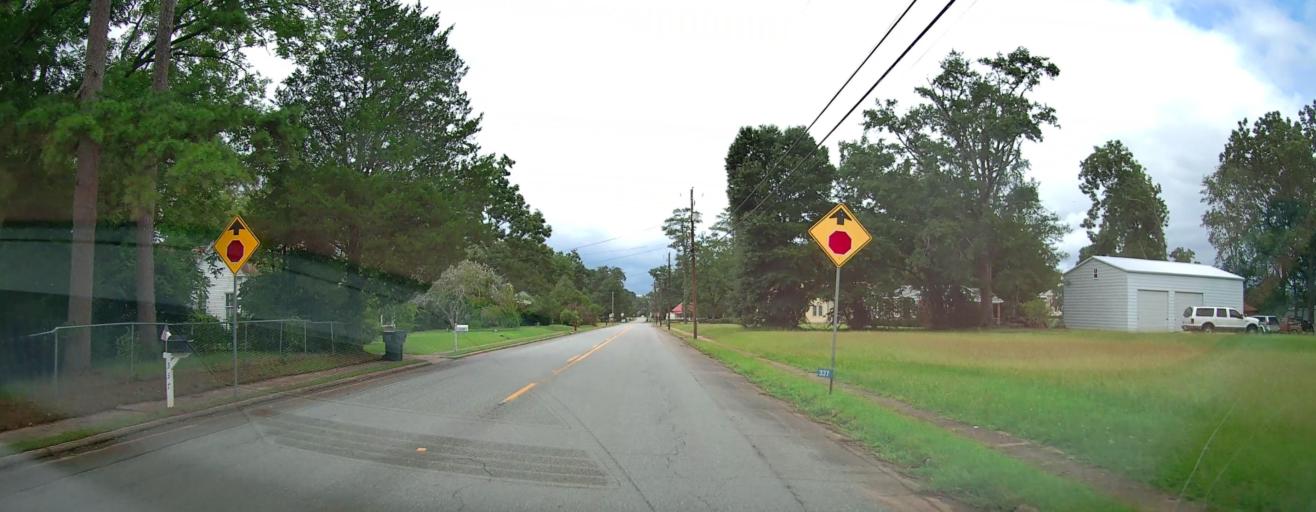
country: US
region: Georgia
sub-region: Twiggs County
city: Jeffersonville
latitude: 32.6858
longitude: -83.3405
